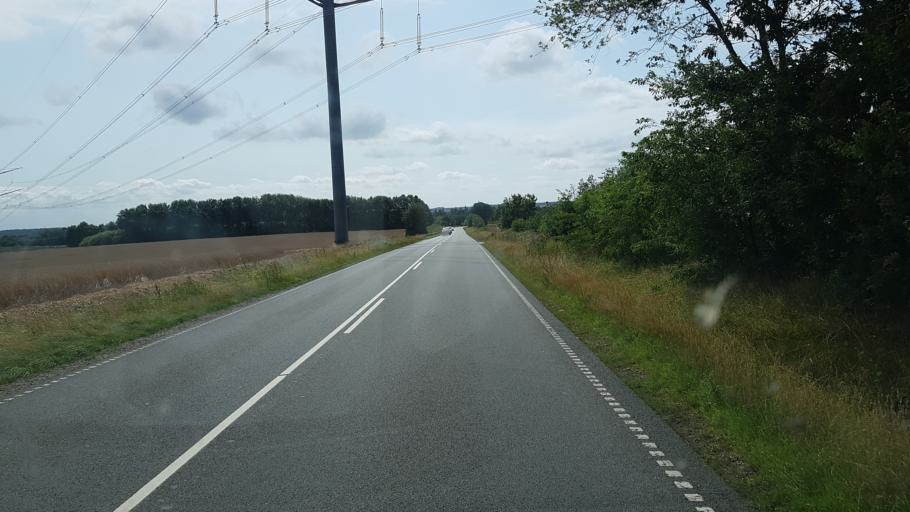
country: DK
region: South Denmark
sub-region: Vejen Kommune
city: Vejen
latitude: 55.5793
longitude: 9.1574
